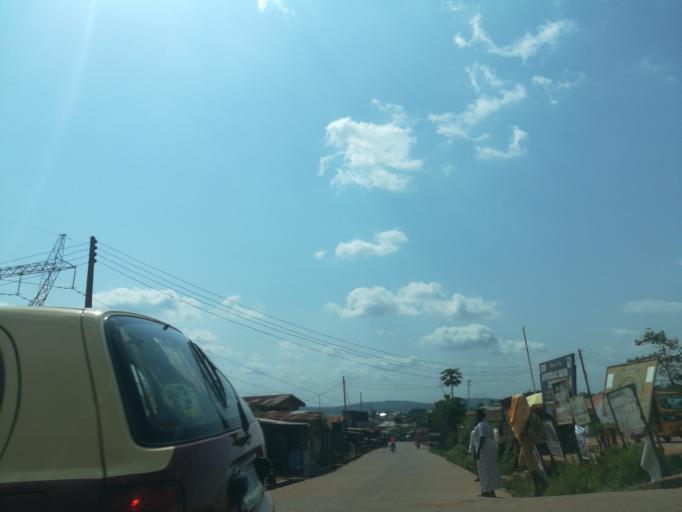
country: NG
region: Oyo
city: Moniya
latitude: 7.5207
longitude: 3.9121
